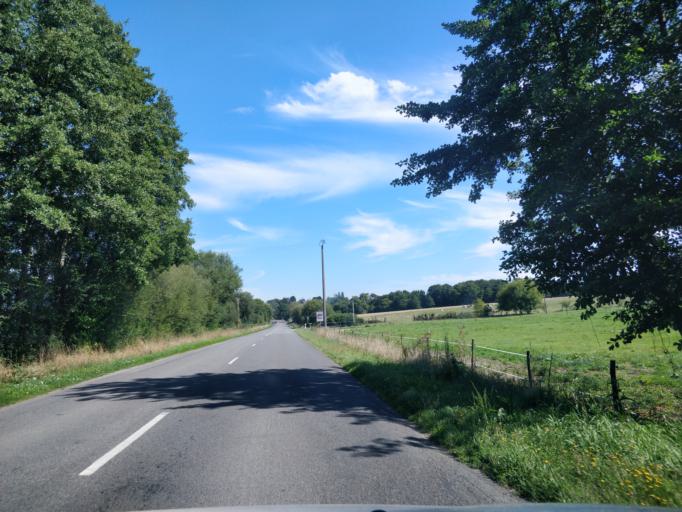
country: FR
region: Pays de la Loire
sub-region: Departement de la Loire-Atlantique
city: Guemene-Penfao
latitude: 47.6215
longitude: -1.8339
